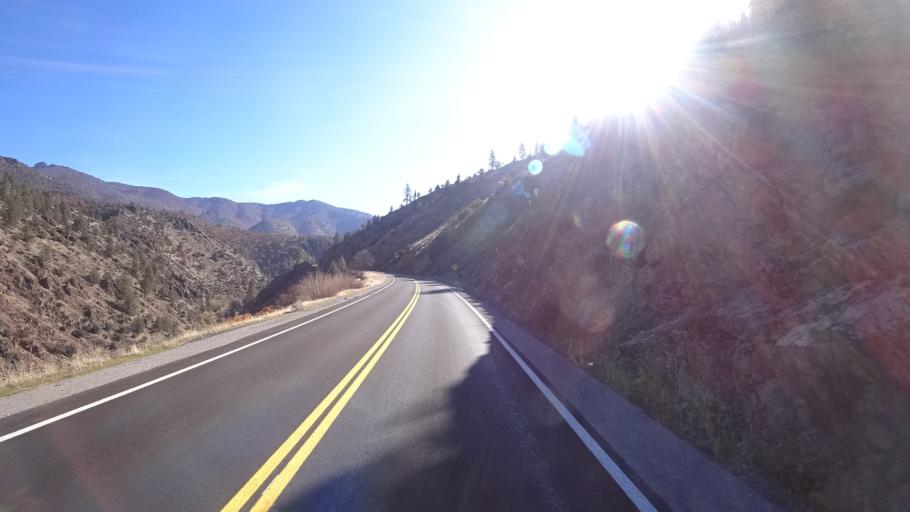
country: US
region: California
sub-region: Siskiyou County
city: Yreka
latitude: 41.8206
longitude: -122.5925
